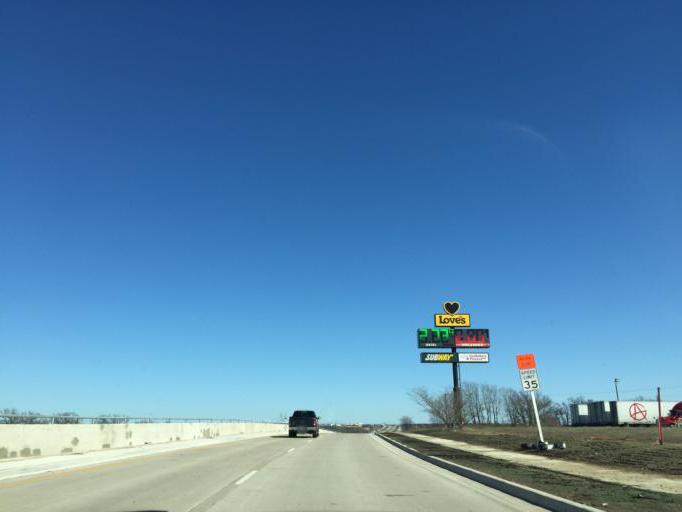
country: US
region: Texas
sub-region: Parker County
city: Hudson Oaks
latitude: 32.7437
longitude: -97.7434
